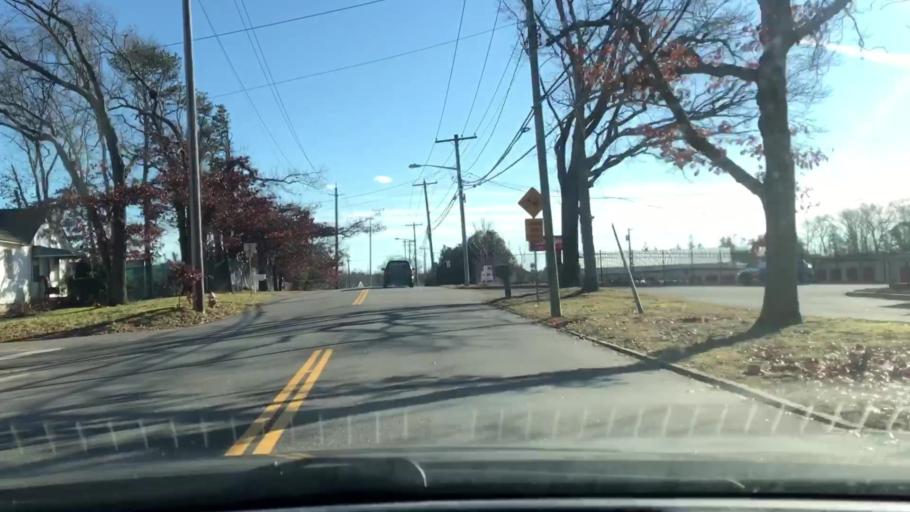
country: US
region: New York
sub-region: Suffolk County
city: Riverhead
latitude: 40.9196
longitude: -72.6909
